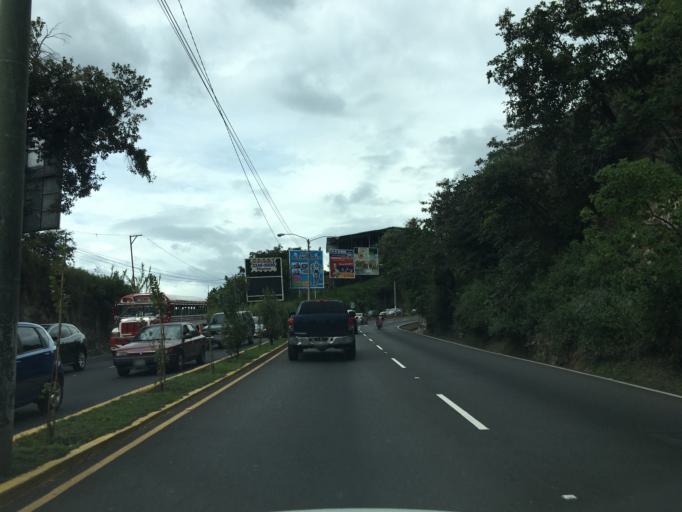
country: GT
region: Guatemala
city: Mixco
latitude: 14.5945
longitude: -90.5705
